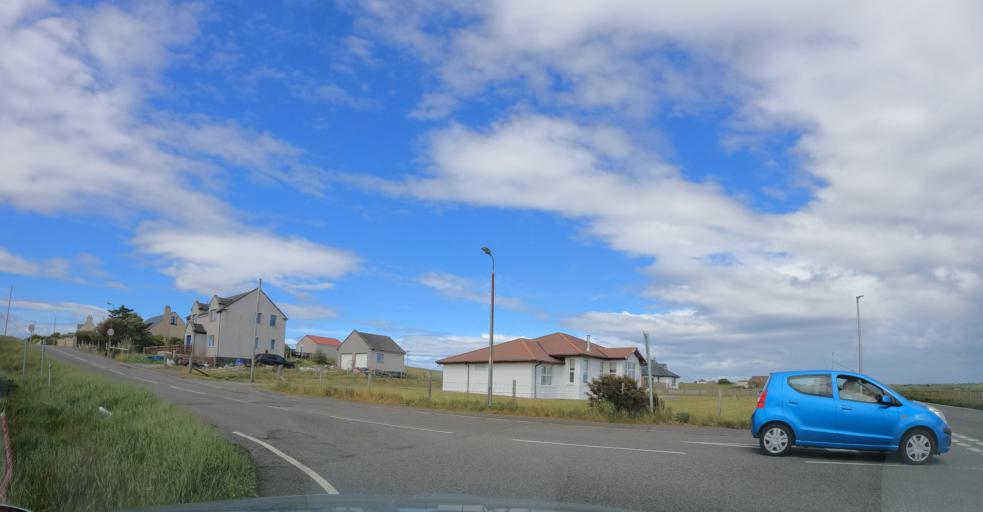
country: GB
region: Scotland
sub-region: Eilean Siar
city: Stornoway
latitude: 58.2041
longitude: -6.3196
